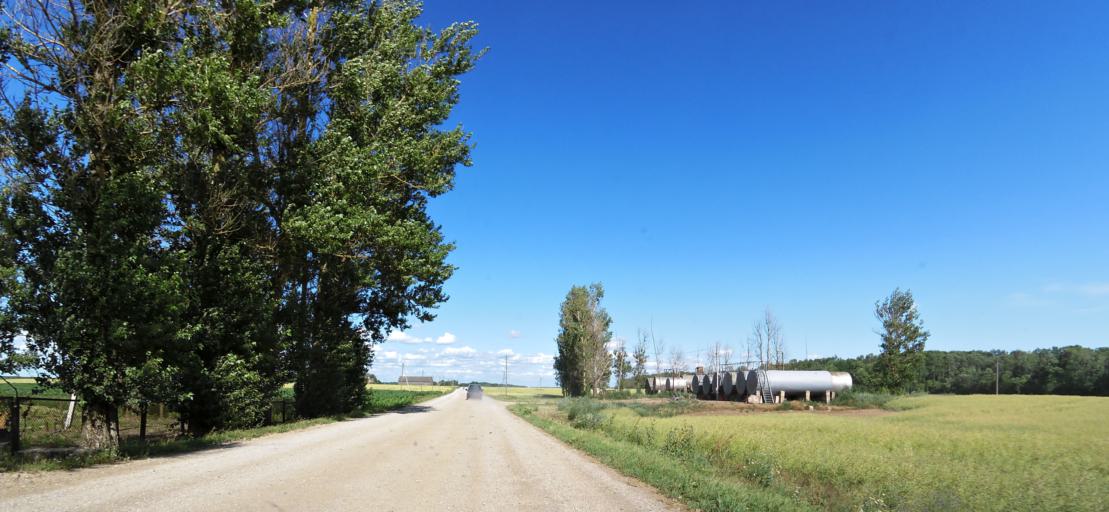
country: LT
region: Panevezys
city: Pasvalys
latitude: 56.1444
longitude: 24.4128
